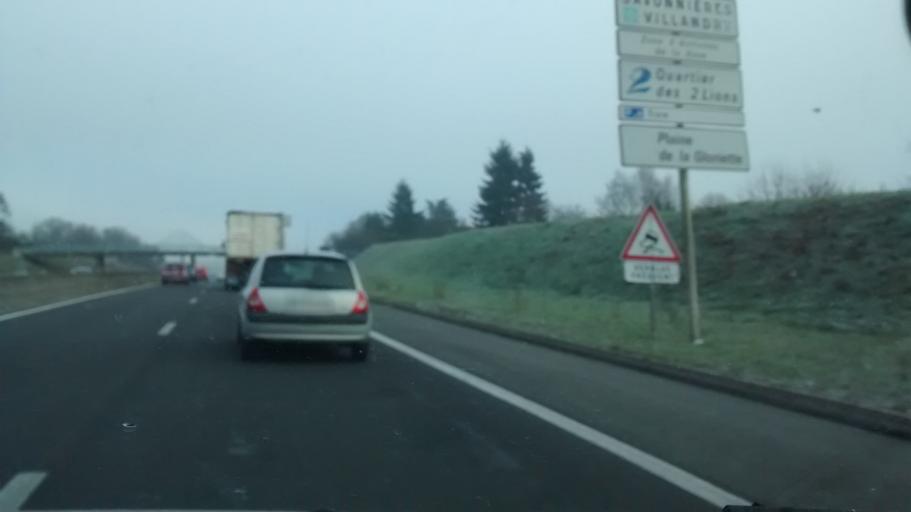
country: FR
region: Centre
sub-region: Departement d'Indre-et-Loire
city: Joue-les-Tours
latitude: 47.3626
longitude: 0.6482
